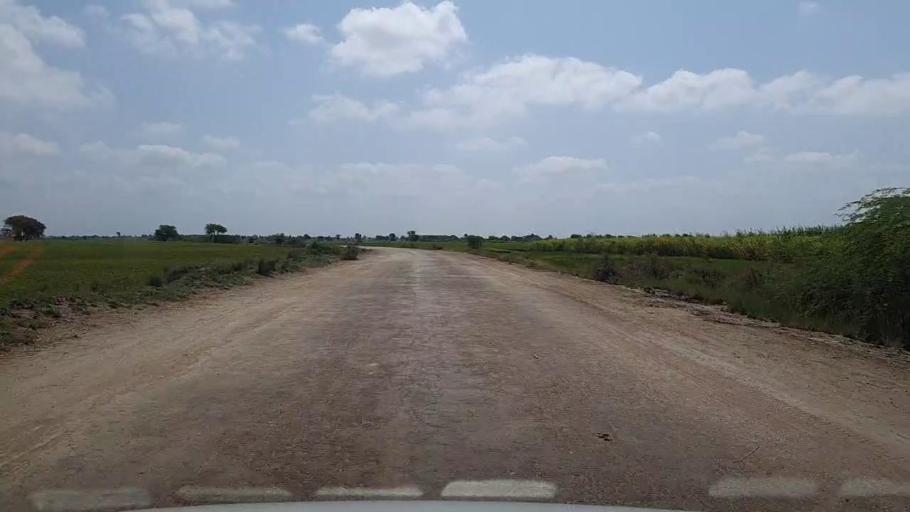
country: PK
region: Sindh
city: Talhar
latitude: 24.8883
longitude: 68.7028
